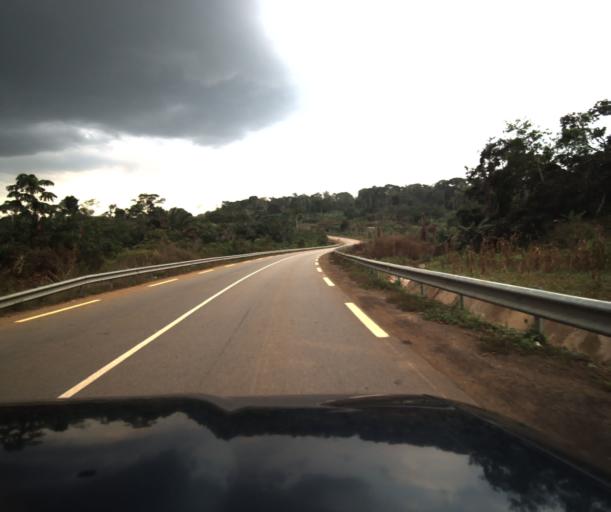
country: CM
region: Centre
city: Mbankomo
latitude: 3.6703
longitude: 11.3467
